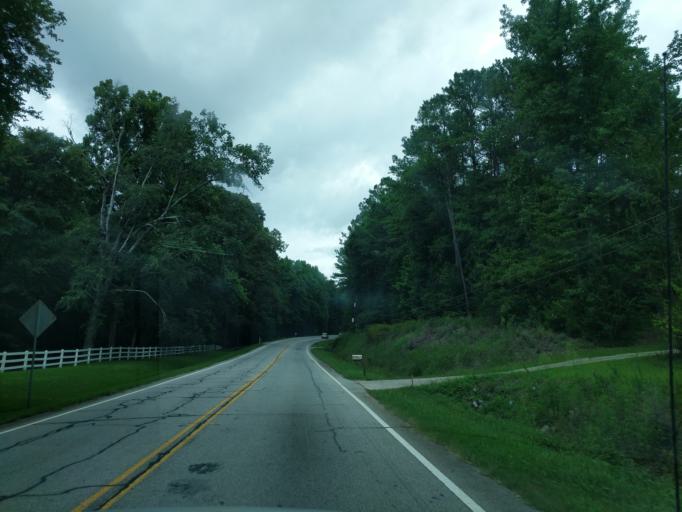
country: US
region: Georgia
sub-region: Walton County
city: Loganville
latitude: 33.8224
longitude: -83.9220
